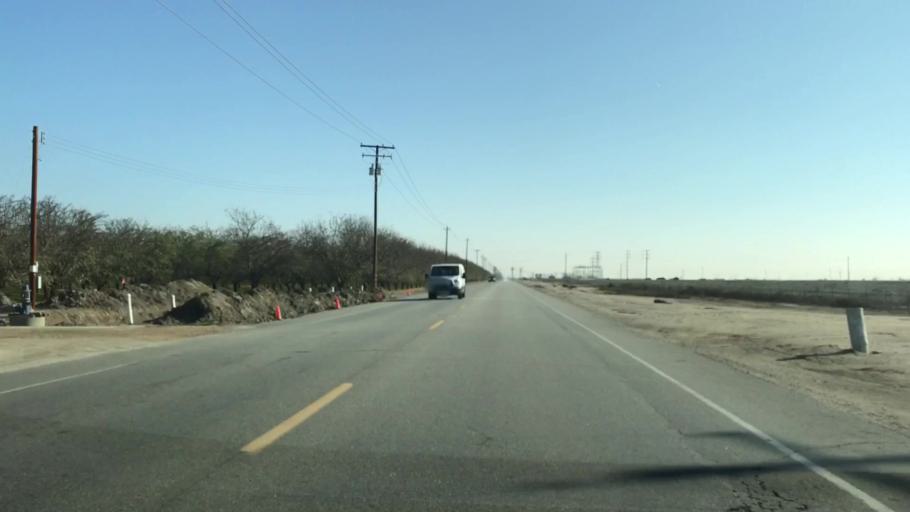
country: US
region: California
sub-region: Kern County
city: Rosedale
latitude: 35.3545
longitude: -119.2792
